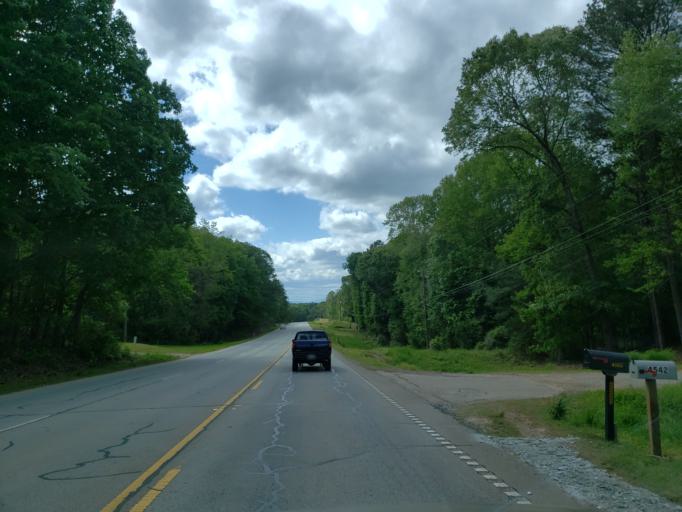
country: US
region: Georgia
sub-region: Haralson County
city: Bremen
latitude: 33.7156
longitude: -85.2194
